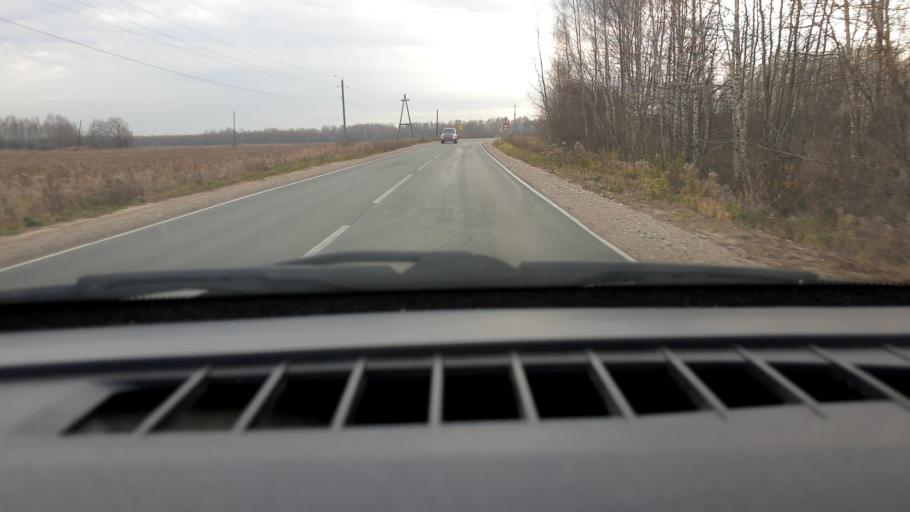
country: RU
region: Nizjnij Novgorod
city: Neklyudovo
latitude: 56.4516
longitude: 43.9020
